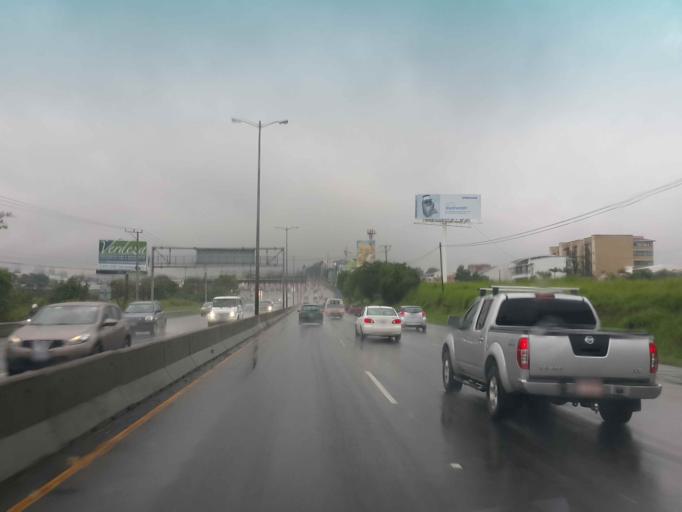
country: CR
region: San Jose
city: San Rafael
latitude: 9.9391
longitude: -84.1401
